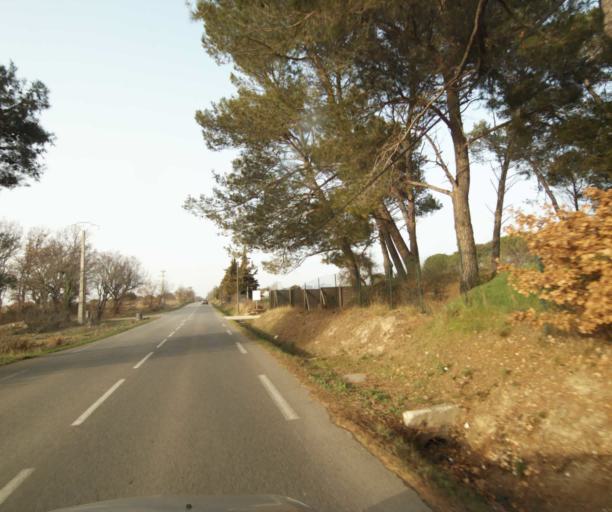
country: FR
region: Provence-Alpes-Cote d'Azur
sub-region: Departement des Bouches-du-Rhone
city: Eguilles
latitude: 43.5936
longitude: 5.3666
